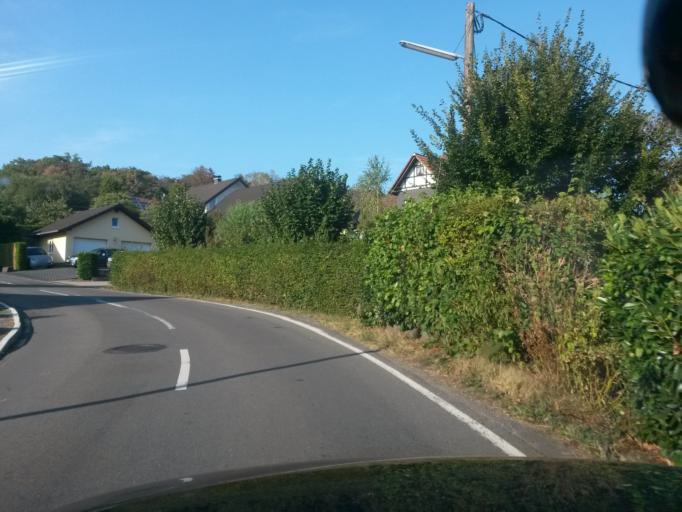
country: DE
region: North Rhine-Westphalia
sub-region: Regierungsbezirk Koln
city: Gummersbach
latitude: 50.9886
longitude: 7.5733
